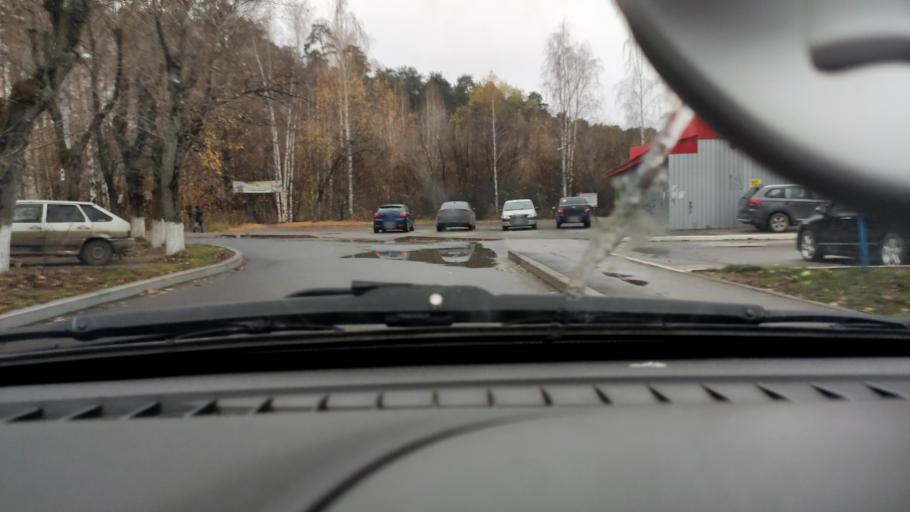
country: RU
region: Perm
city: Kultayevo
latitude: 58.0125
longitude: 55.9663
